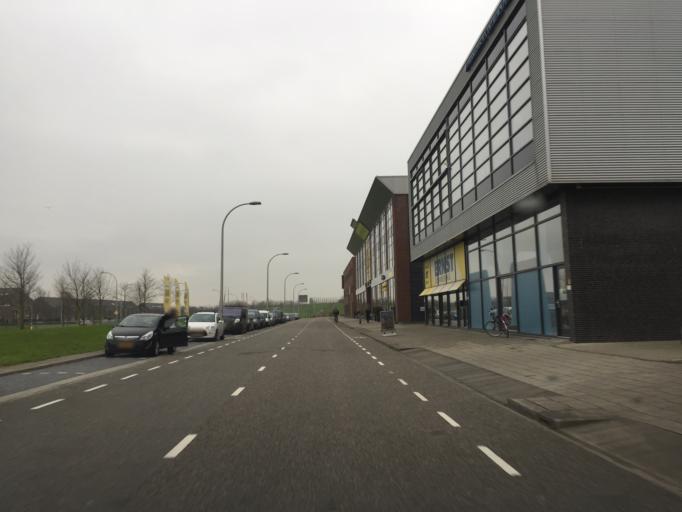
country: NL
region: South Holland
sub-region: Gemeente Den Haag
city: Ypenburg
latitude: 52.0398
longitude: 4.3586
